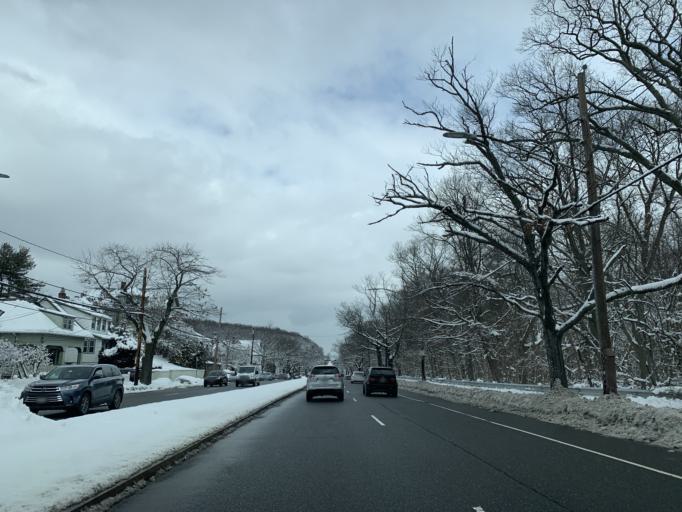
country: US
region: Massachusetts
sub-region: Norfolk County
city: Dedham
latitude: 42.2702
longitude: -71.1471
